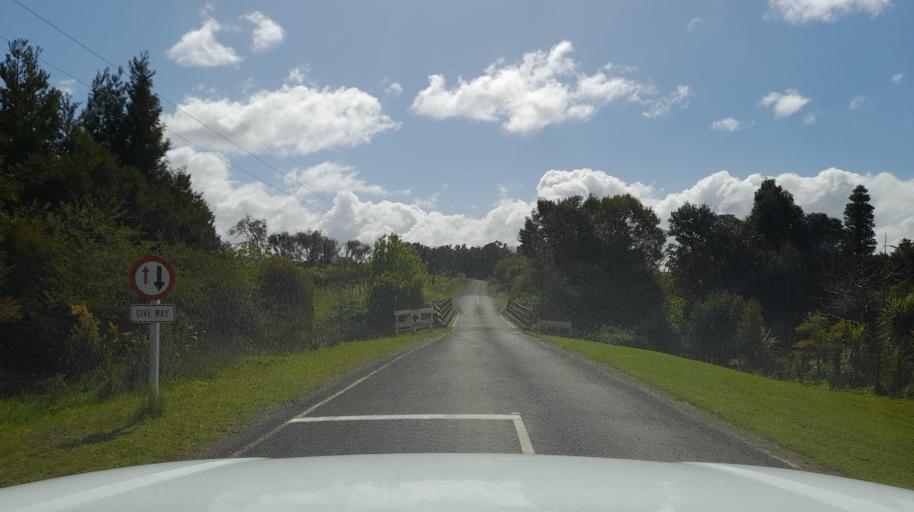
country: NZ
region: Northland
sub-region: Far North District
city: Kerikeri
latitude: -35.2290
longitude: 173.8763
